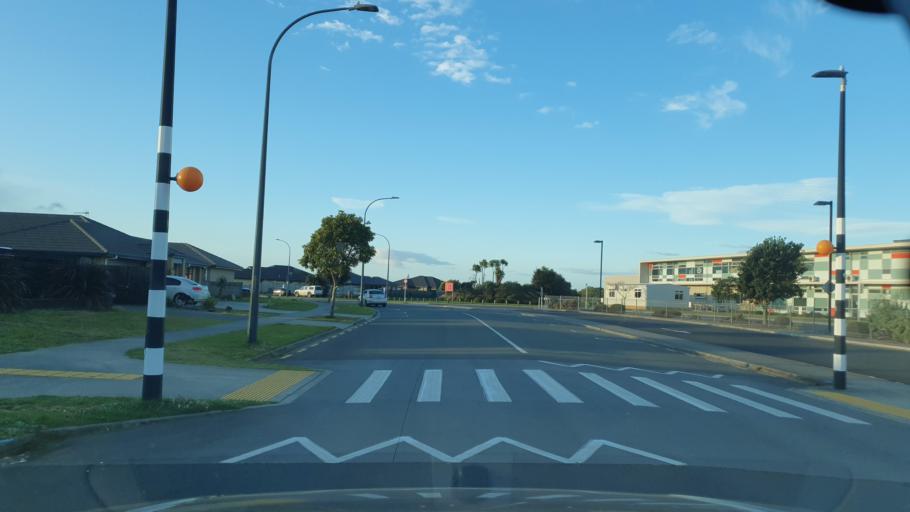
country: NZ
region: Bay of Plenty
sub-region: Tauranga City
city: Tauranga
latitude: -37.7116
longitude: 176.3007
